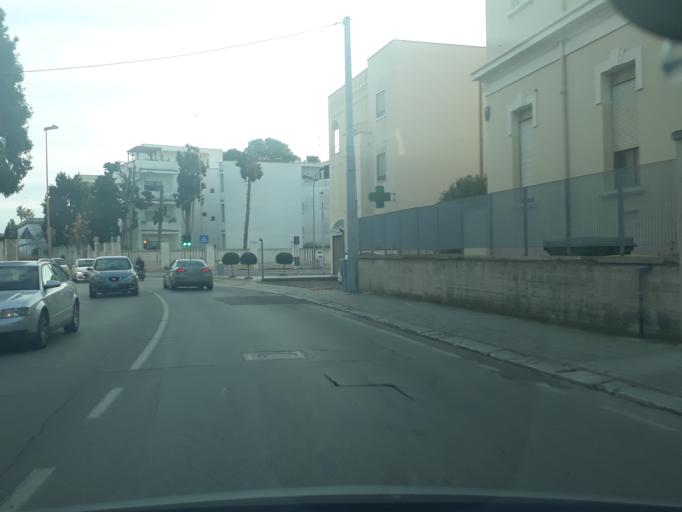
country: IT
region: Apulia
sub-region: Provincia di Brindisi
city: Materdomini
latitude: 40.6485
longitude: 17.9440
